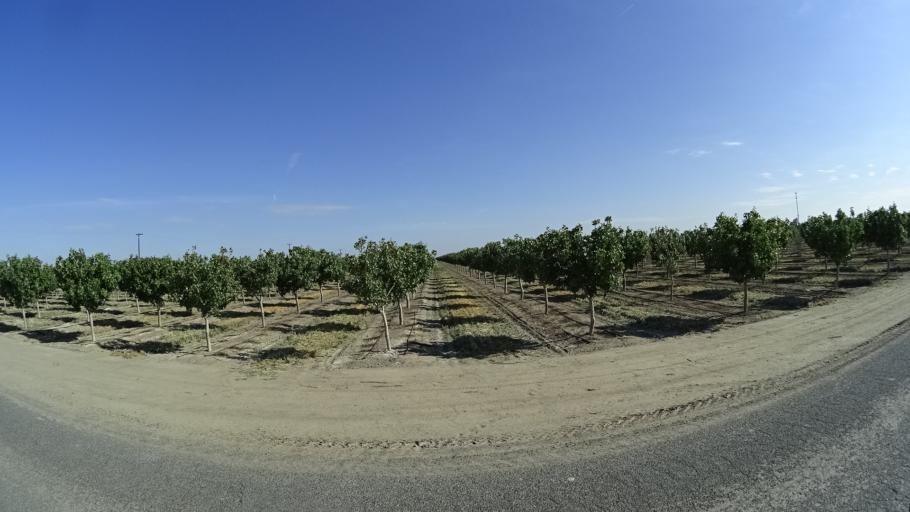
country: US
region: California
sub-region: Kings County
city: Stratford
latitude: 36.2259
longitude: -119.7975
